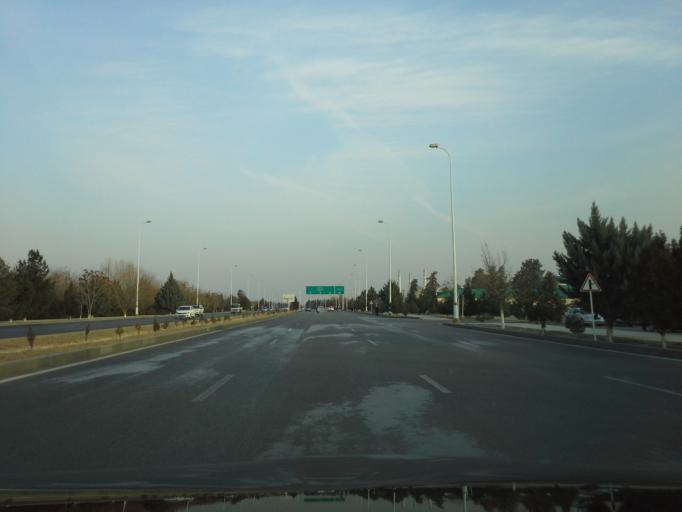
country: TM
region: Ahal
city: Abadan
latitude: 38.0267
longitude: 58.2385
